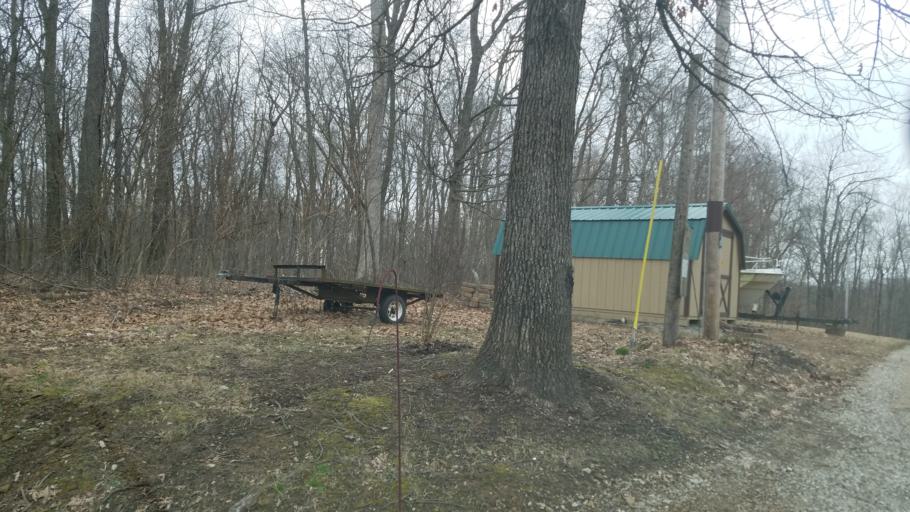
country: US
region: Ohio
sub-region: Licking County
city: Utica
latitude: 40.2064
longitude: -82.3929
